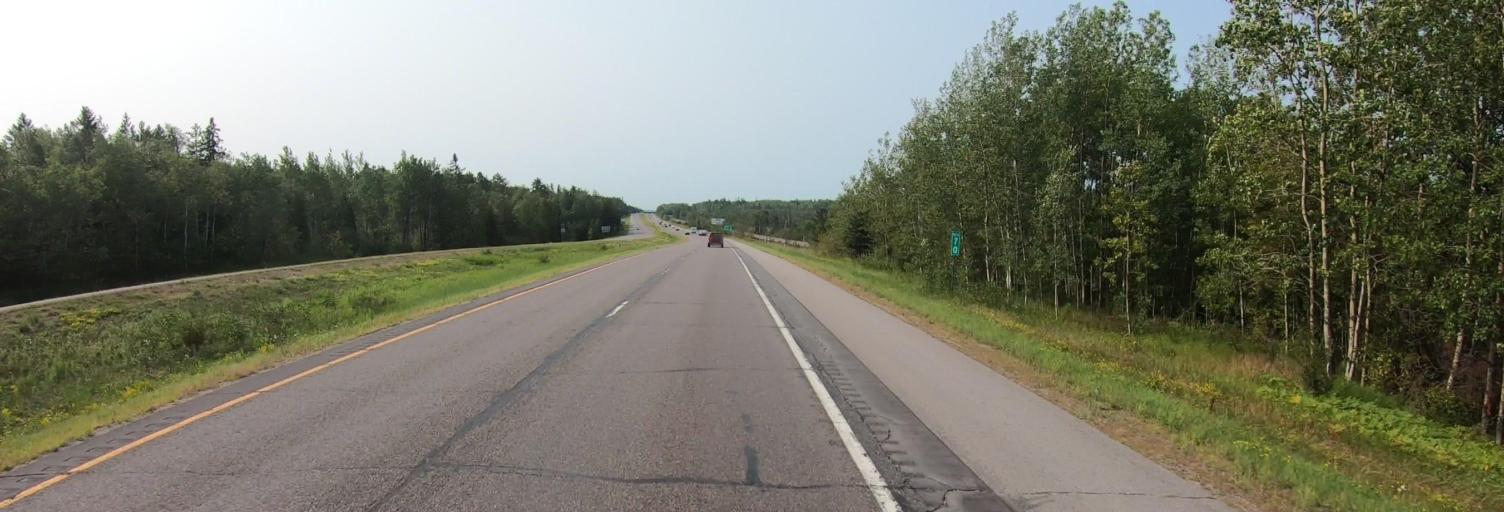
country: US
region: Minnesota
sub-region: Saint Louis County
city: Virginia
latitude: 47.5767
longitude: -92.5448
